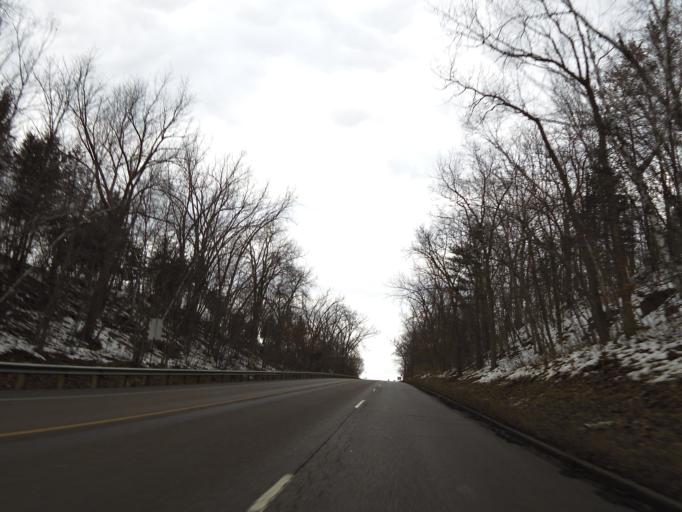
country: US
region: Minnesota
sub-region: Washington County
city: Stillwater
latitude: 45.0609
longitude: -92.7947
